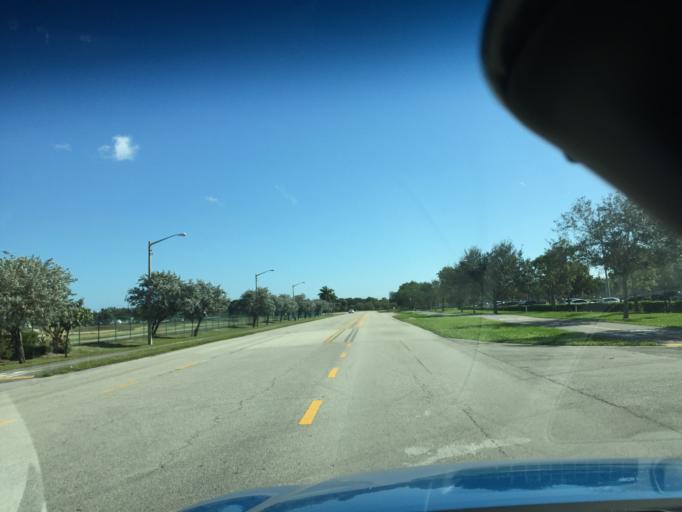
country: US
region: Florida
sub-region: Broward County
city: Pompano Beach
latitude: 26.2414
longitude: -80.1087
